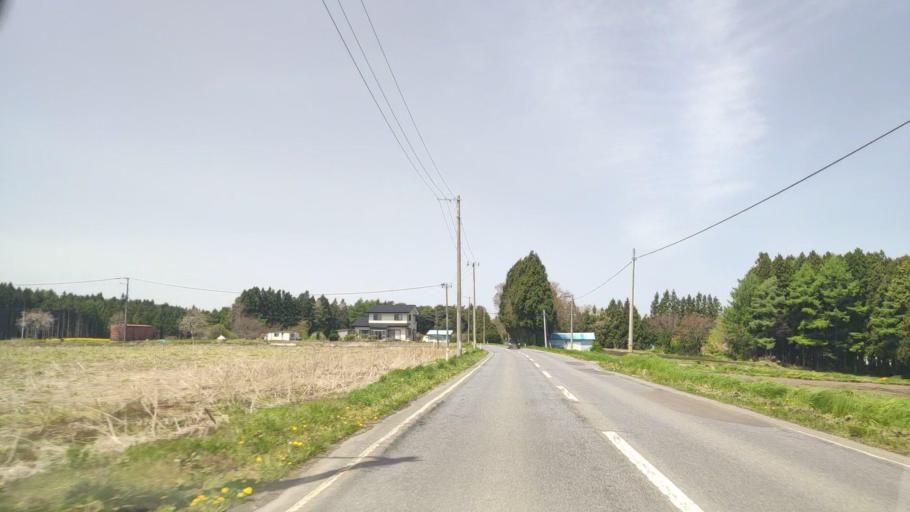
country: JP
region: Aomori
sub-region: Hachinohe Shi
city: Uchimaru
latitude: 40.5308
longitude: 141.4053
